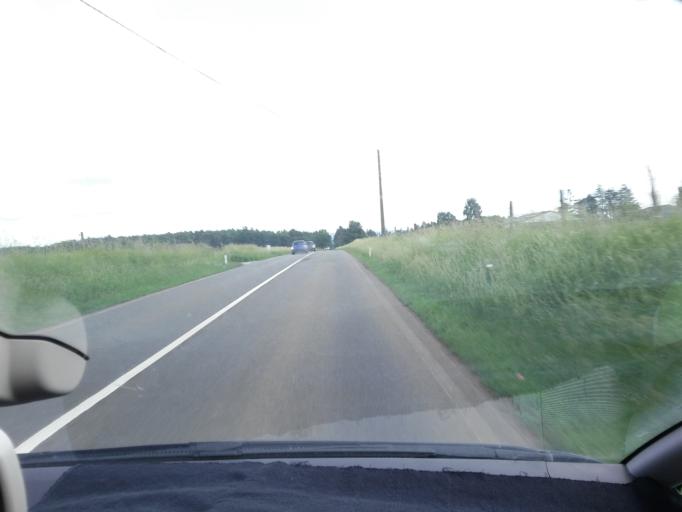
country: BE
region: Wallonia
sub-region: Province de Namur
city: Rochefort
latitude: 50.1374
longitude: 5.2261
